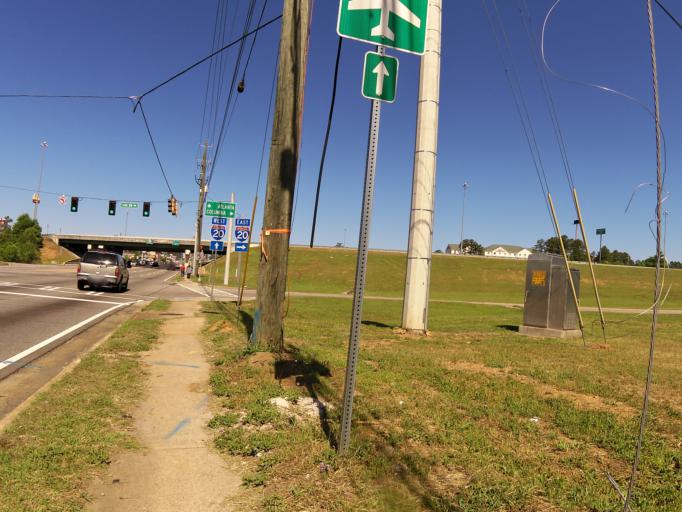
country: US
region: Georgia
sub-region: Columbia County
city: Martinez
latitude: 33.5120
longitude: -82.0411
